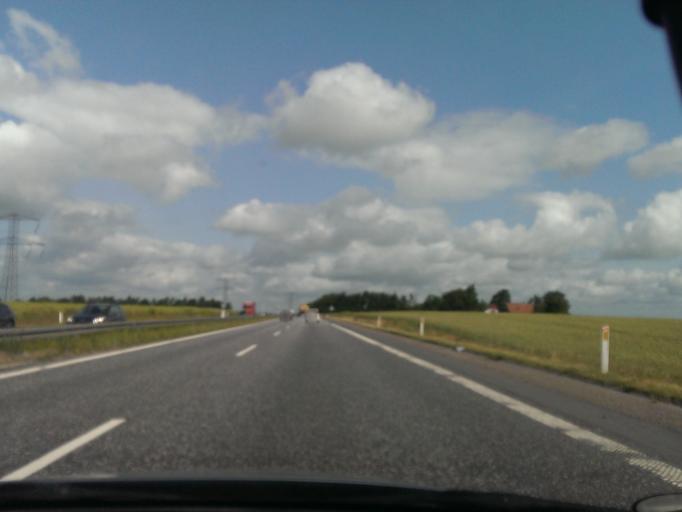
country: DK
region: Central Jutland
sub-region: Randers Kommune
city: Randers
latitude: 56.4962
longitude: 9.9794
